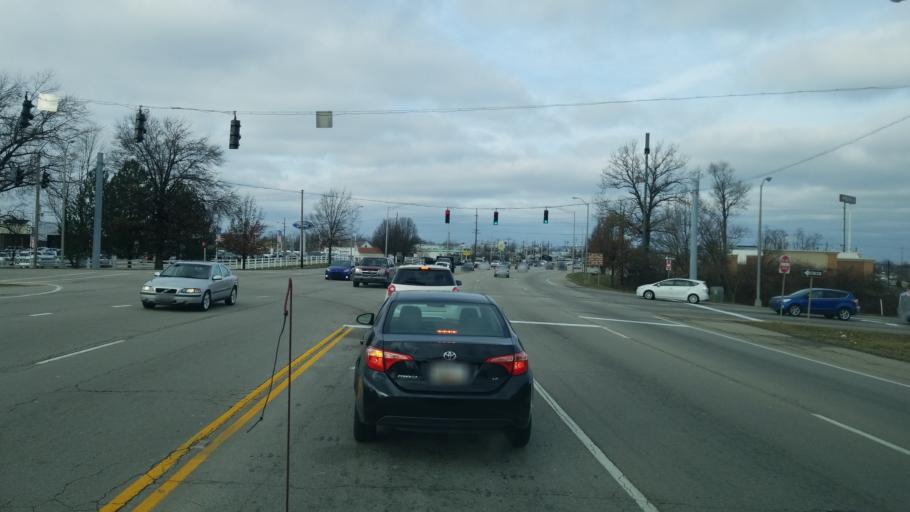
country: US
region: Kentucky
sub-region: Boone County
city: Florence
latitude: 39.0016
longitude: -84.6486
